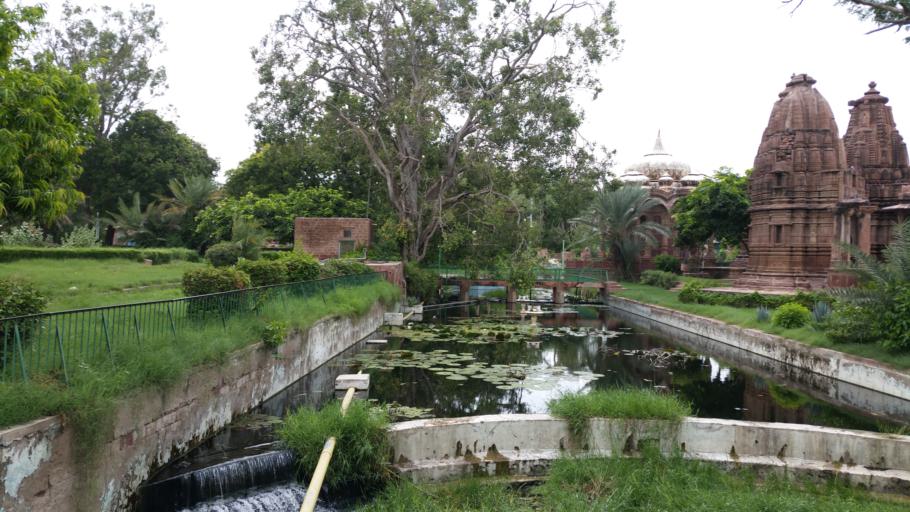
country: IN
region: Rajasthan
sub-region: Jodhpur
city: Jodhpur
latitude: 26.3516
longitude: 73.0352
